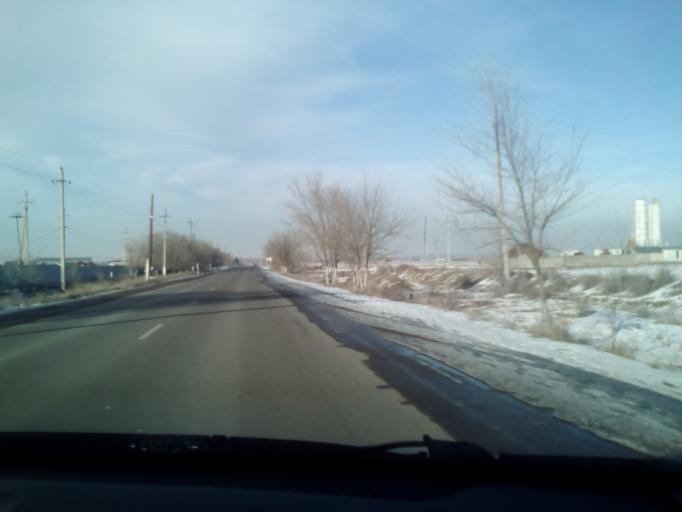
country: KZ
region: Almaty Oblysy
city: Burunday
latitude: 43.1941
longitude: 76.4148
